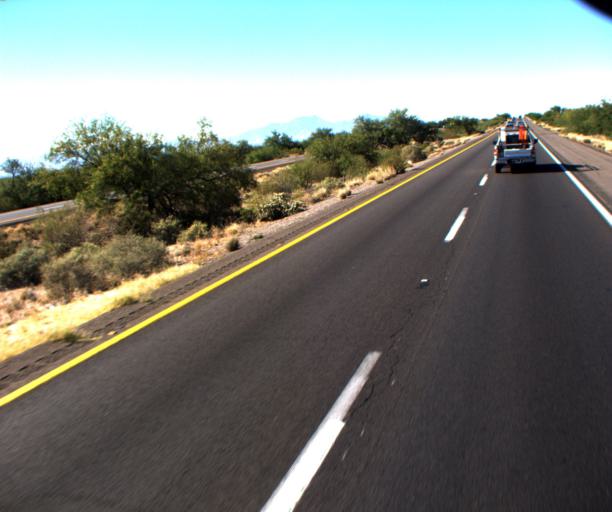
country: US
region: Arizona
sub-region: Pima County
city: Summit
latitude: 32.0573
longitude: -110.9931
